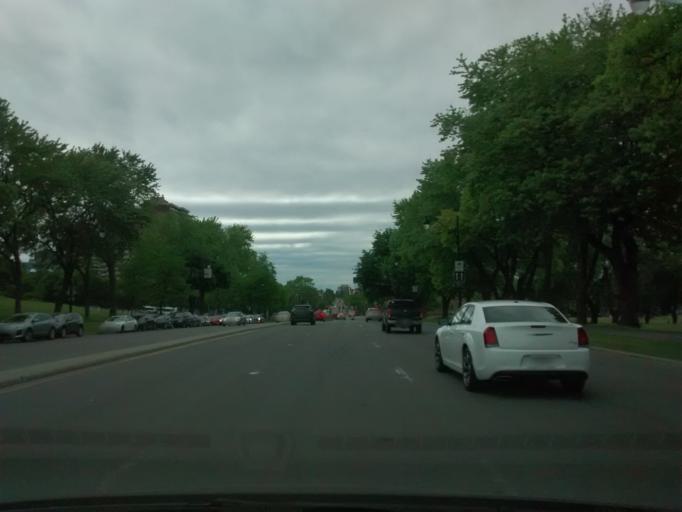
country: CA
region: Quebec
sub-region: Montreal
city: Montreal
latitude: 45.5151
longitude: -73.5857
